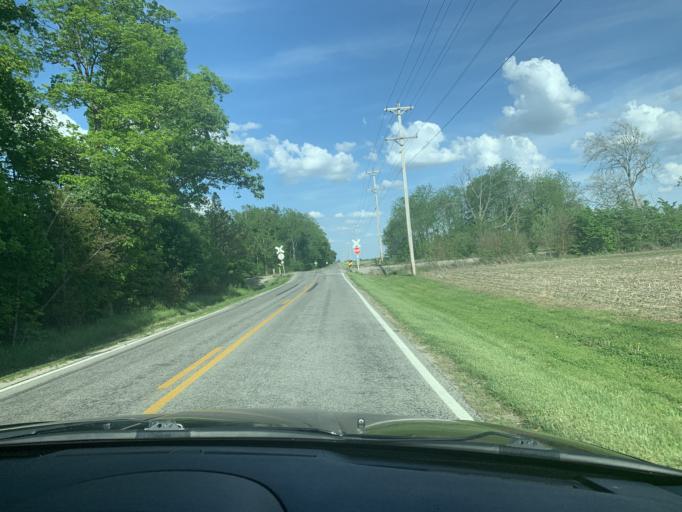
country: US
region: Ohio
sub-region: Logan County
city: De Graff
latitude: 40.2415
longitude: -83.9684
